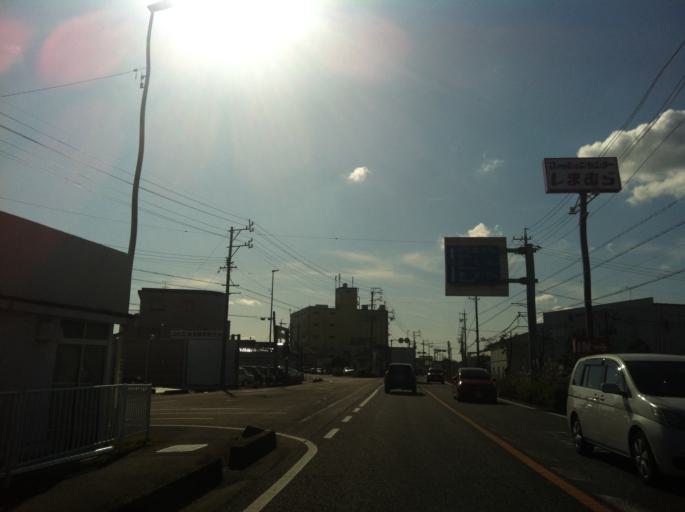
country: JP
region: Shizuoka
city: Fujieda
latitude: 34.8918
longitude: 138.2809
